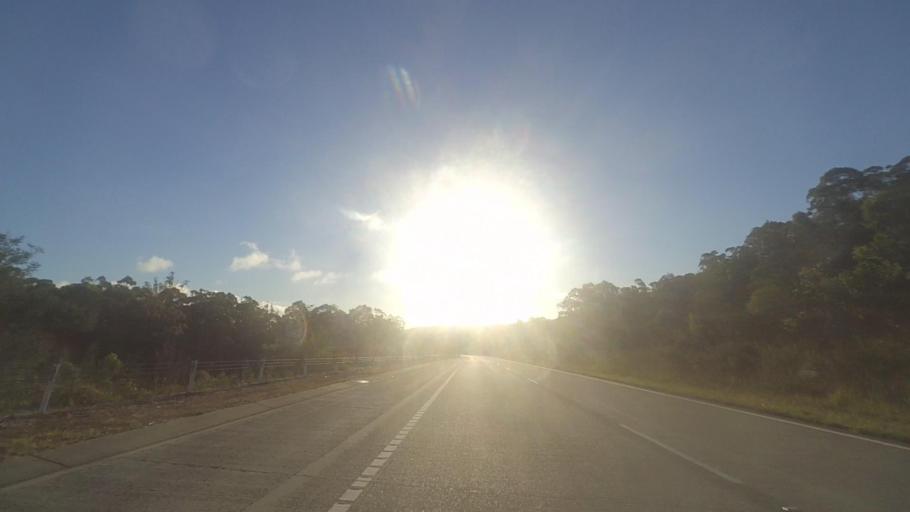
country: AU
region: New South Wales
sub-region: Great Lakes
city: Hawks Nest
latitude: -32.5365
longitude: 152.1750
